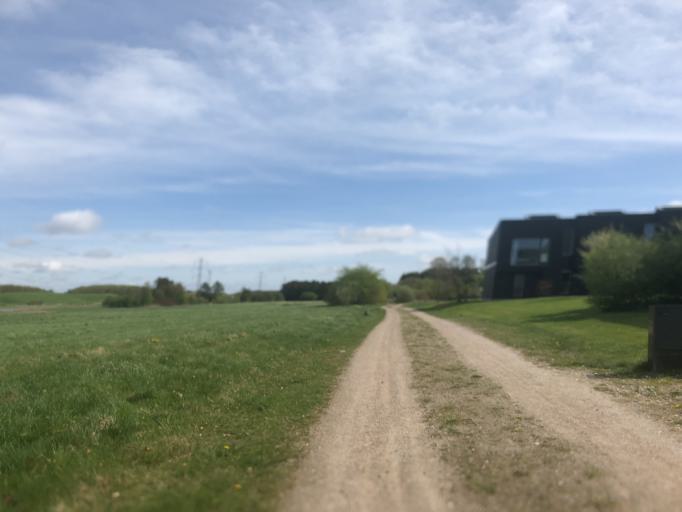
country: DK
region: Zealand
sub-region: Ringsted Kommune
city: Ringsted
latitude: 55.4522
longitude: 11.8113
